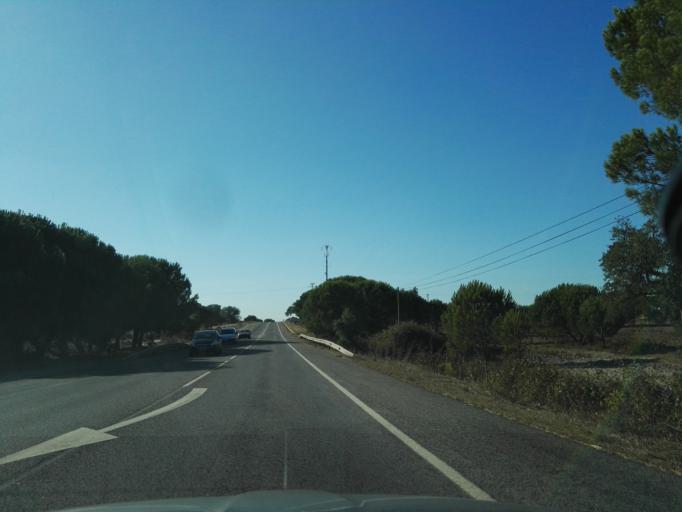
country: PT
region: Santarem
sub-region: Benavente
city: Poceirao
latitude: 38.8416
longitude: -8.7429
